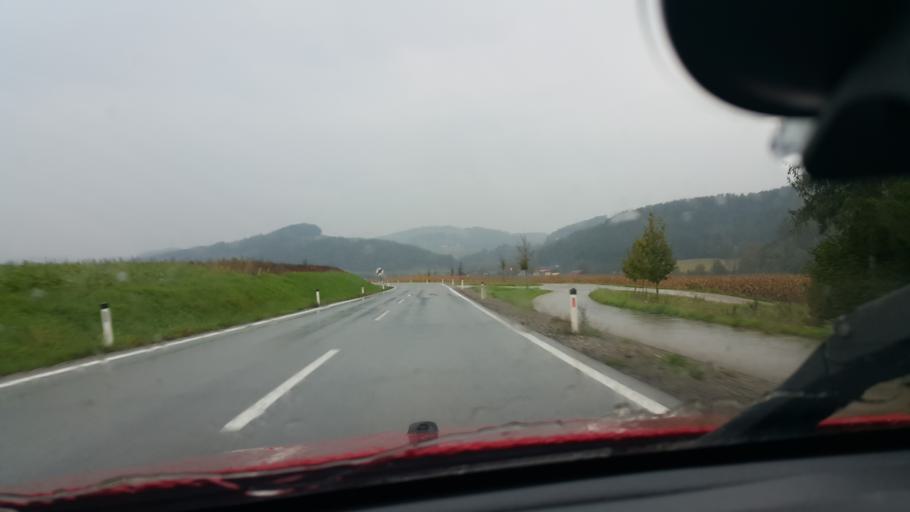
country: AT
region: Carinthia
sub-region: Politischer Bezirk Volkermarkt
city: Ruden
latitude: 46.6661
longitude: 14.7705
